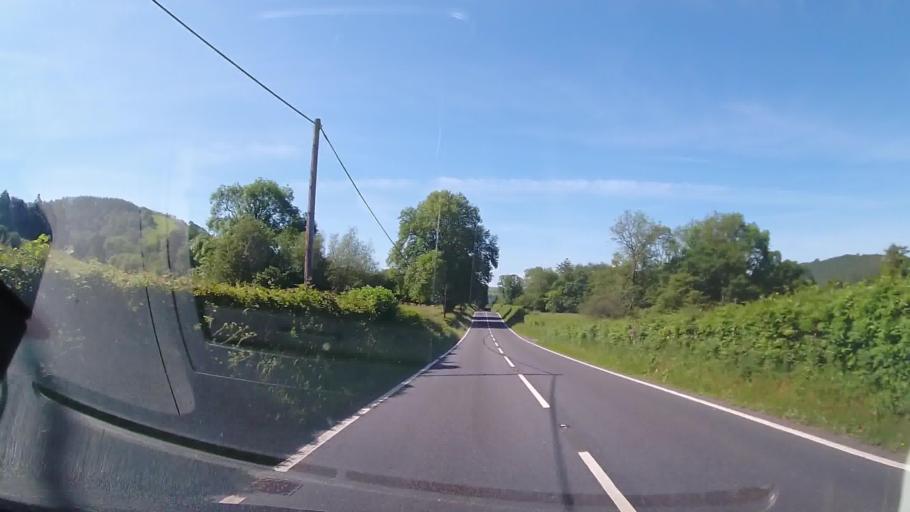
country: GB
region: Wales
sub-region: Gwynedd
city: Corris
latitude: 52.6509
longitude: -3.7067
